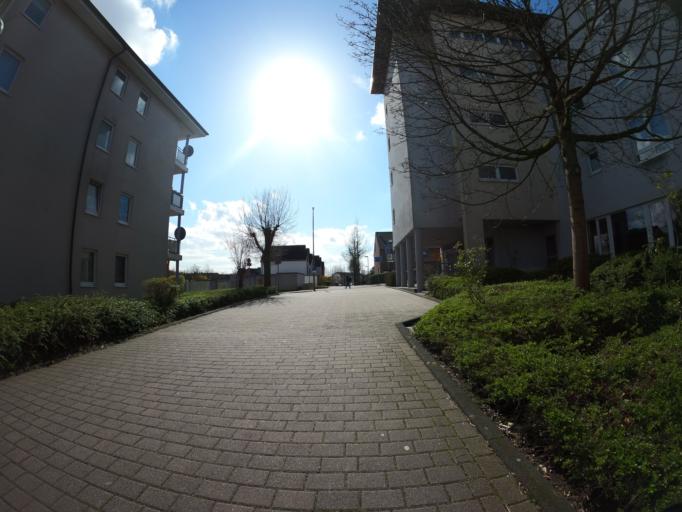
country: DE
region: North Rhine-Westphalia
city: Wulfrath
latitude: 51.2346
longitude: 7.0647
